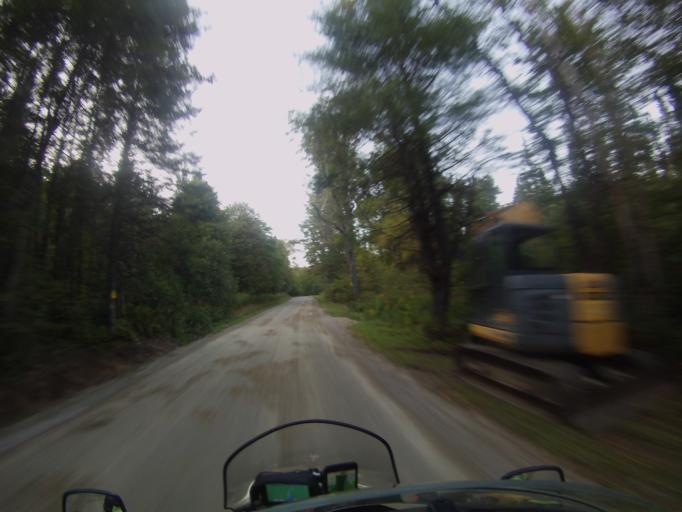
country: US
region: Vermont
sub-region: Addison County
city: Bristol
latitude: 44.0104
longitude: -73.0225
